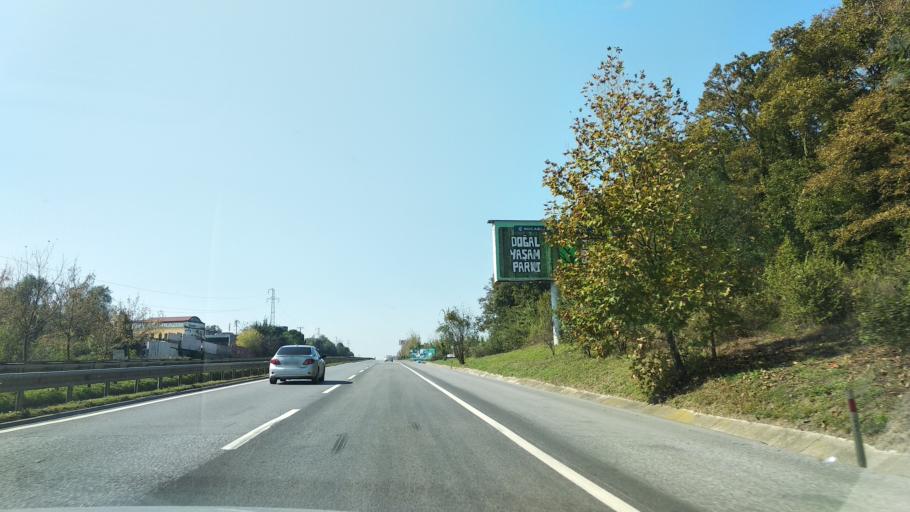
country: TR
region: Kocaeli
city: Derbent
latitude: 40.7313
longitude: 30.1657
